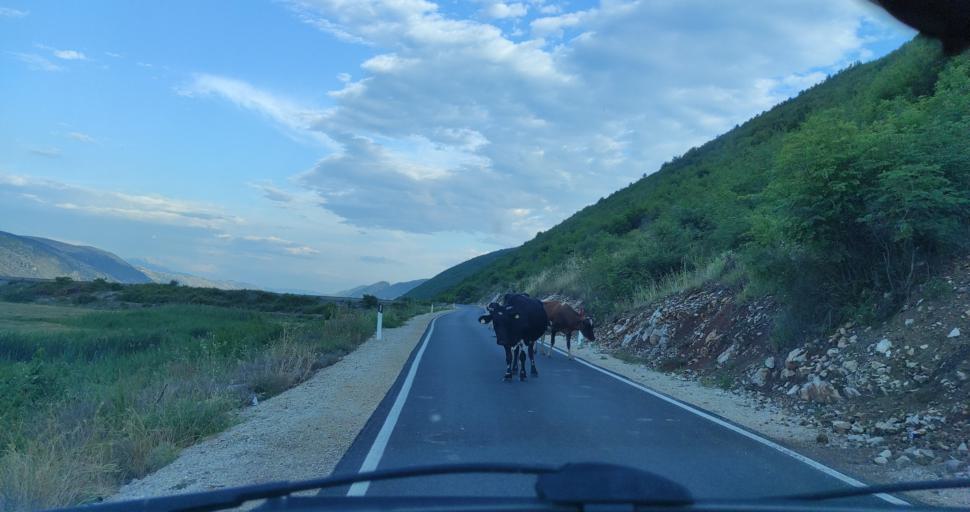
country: AL
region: Shkoder
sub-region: Rrethi i Shkodres
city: Velipoje
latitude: 41.9232
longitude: 19.4518
